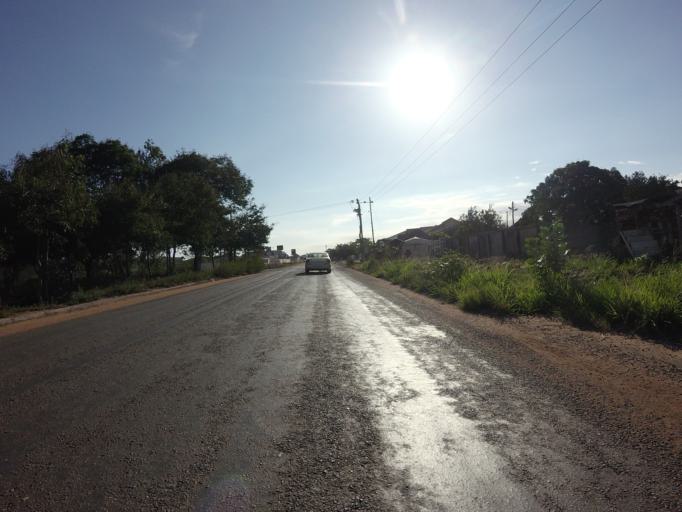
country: GH
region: Greater Accra
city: Nungua
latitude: 5.6503
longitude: -0.0718
